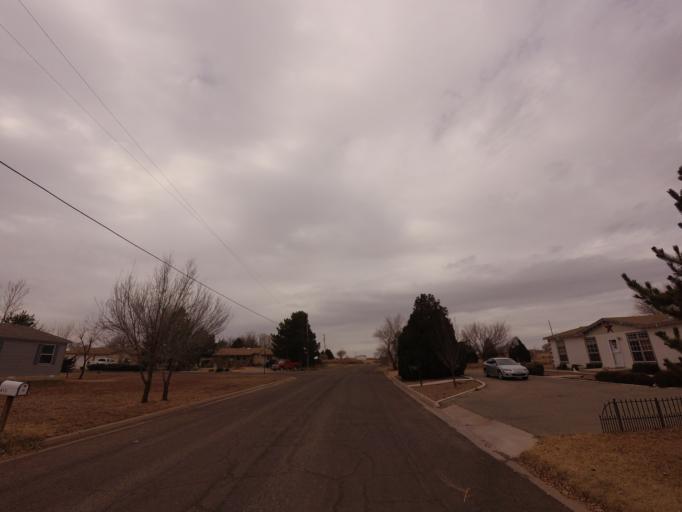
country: US
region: New Mexico
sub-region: Curry County
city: Clovis
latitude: 34.3801
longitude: -103.2018
